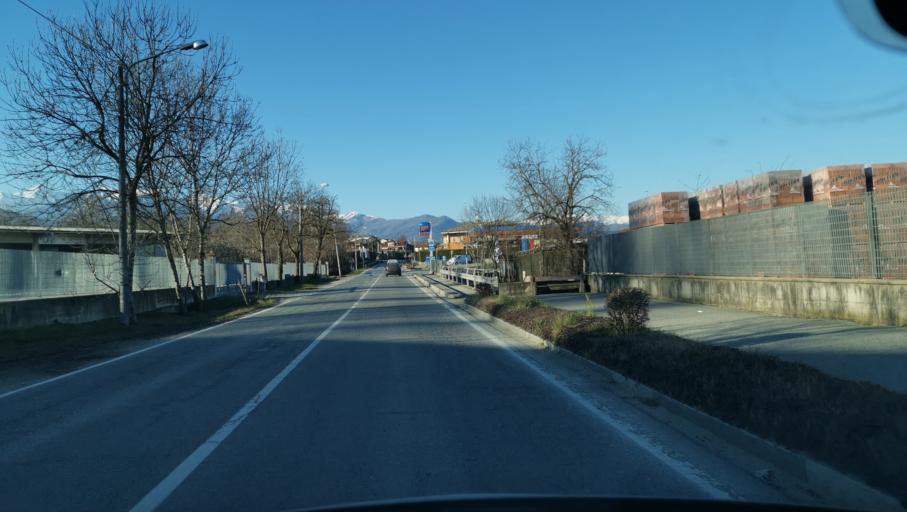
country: IT
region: Piedmont
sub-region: Provincia di Cuneo
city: Bagnolo Piemonte
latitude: 44.7662
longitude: 7.3107
